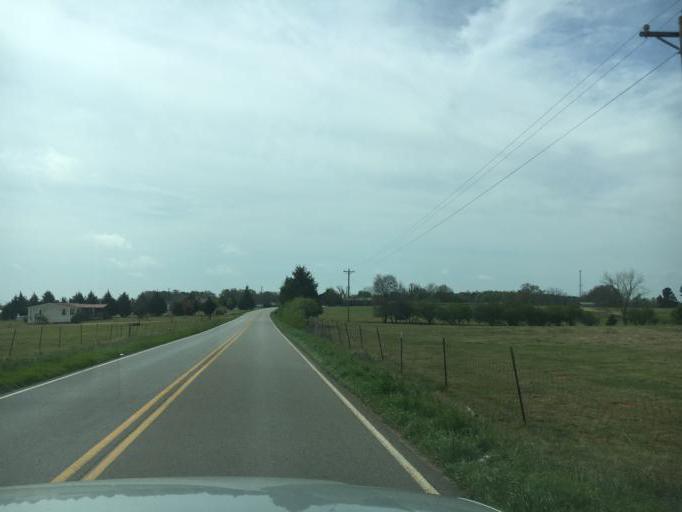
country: US
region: Georgia
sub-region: Hart County
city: Royston
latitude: 34.2994
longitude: -83.0443
